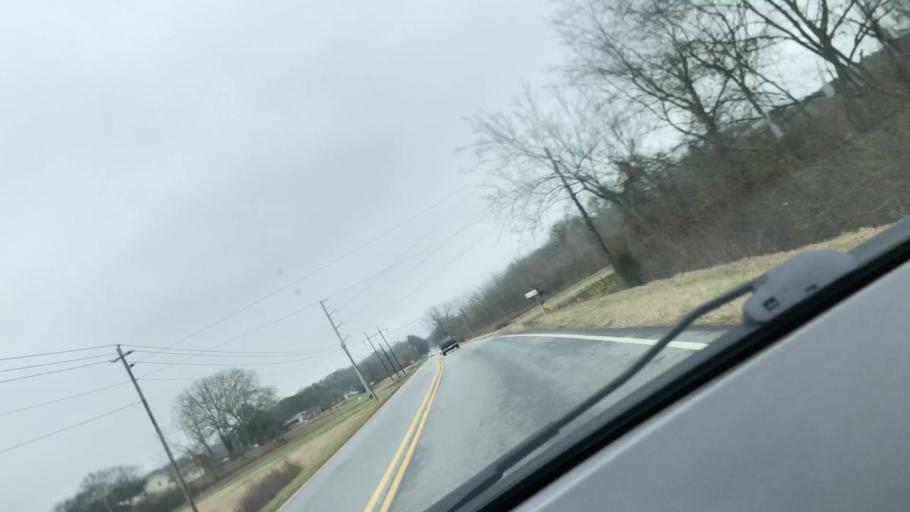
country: US
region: Georgia
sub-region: Bartow County
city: Cartersville
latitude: 34.1713
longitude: -84.8288
